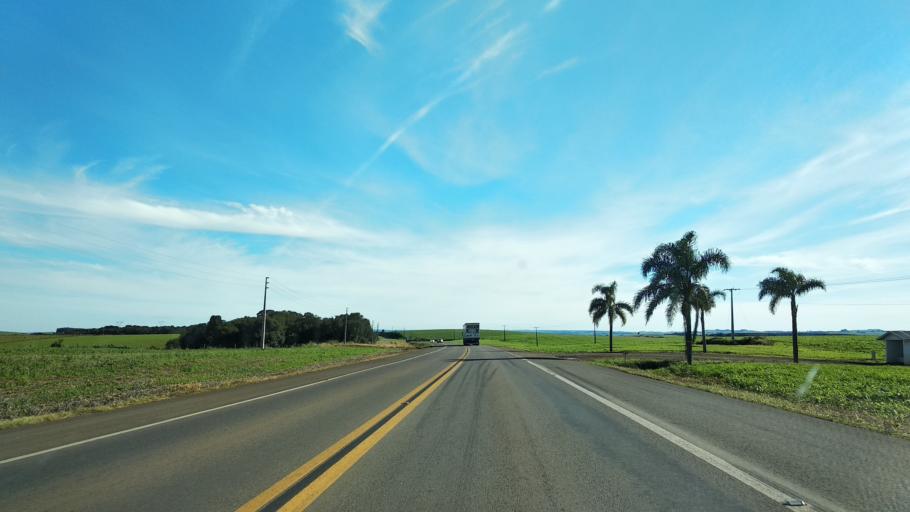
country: BR
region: Santa Catarina
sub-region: Campos Novos
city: Campos Novos
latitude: -27.4906
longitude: -51.3300
